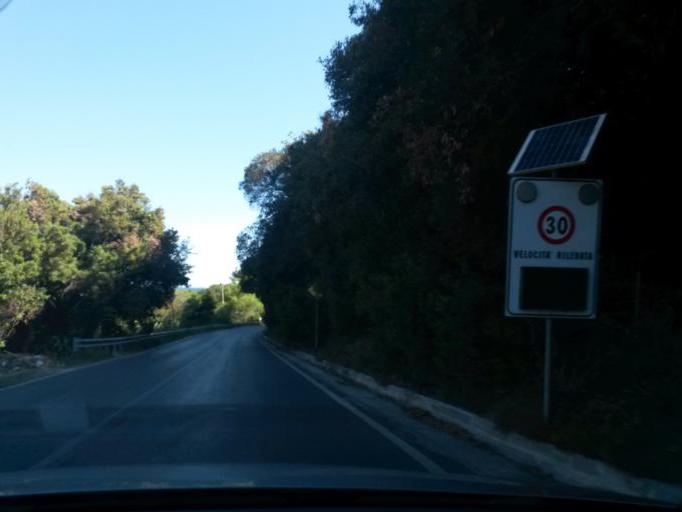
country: IT
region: Tuscany
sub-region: Provincia di Livorno
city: Campo nell'Elba
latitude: 42.7813
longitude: 10.2451
